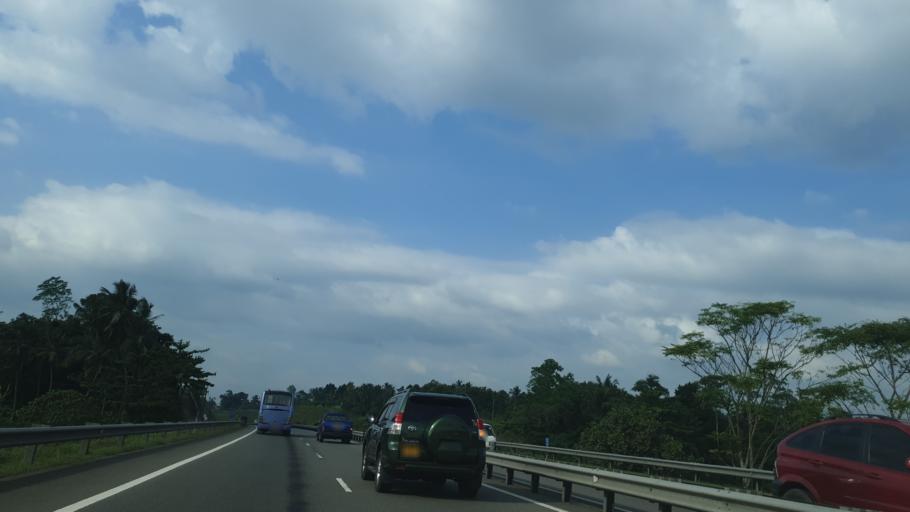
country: LK
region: Western
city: Horana South
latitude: 6.7438
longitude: 79.9978
